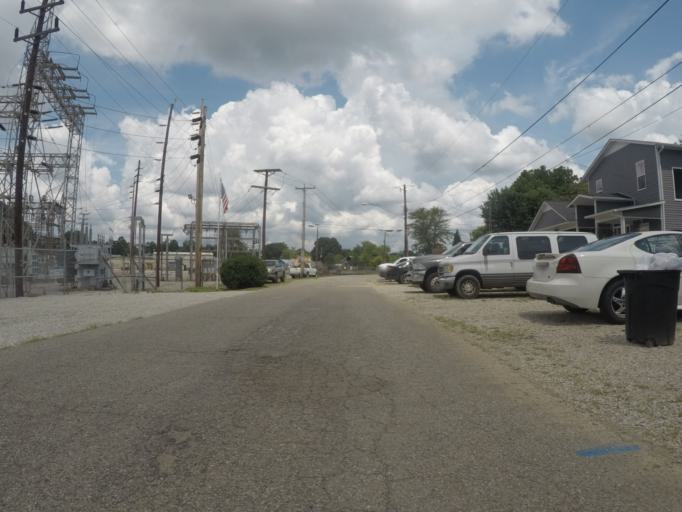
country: US
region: West Virginia
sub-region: Cabell County
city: Huntington
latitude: 38.4200
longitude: -82.3859
